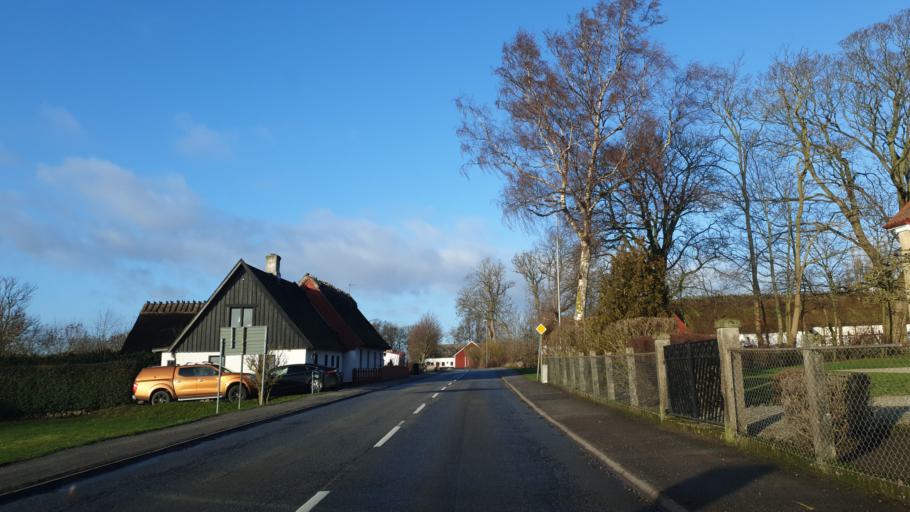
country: SE
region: Skane
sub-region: Vellinge Kommun
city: Vellinge
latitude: 55.5017
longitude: 13.0308
